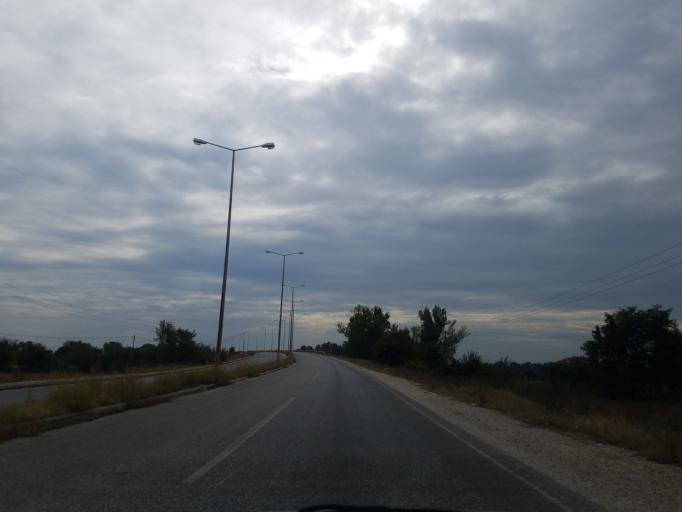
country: GR
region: Thessaly
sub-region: Trikala
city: Pyrgetos
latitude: 39.5221
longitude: 21.7532
